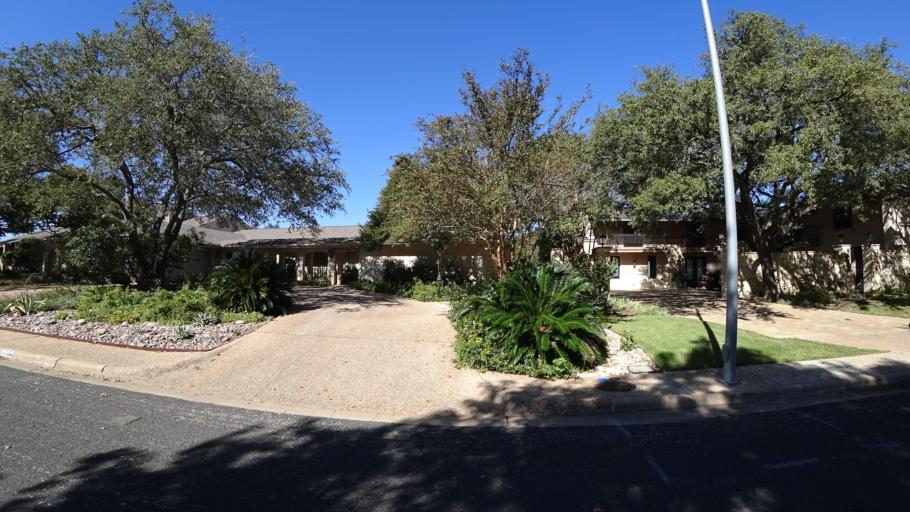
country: US
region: Texas
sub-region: Travis County
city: West Lake Hills
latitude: 30.3525
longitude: -97.7804
